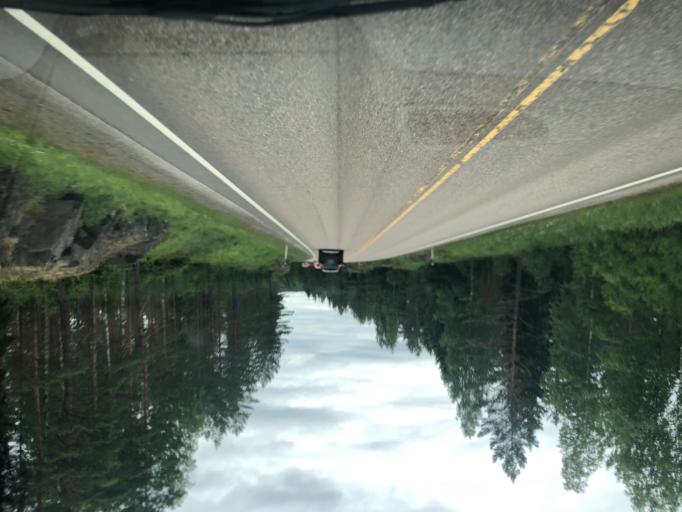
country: FI
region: Southern Savonia
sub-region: Mikkeli
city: Maentyharju
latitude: 61.1516
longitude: 27.1392
